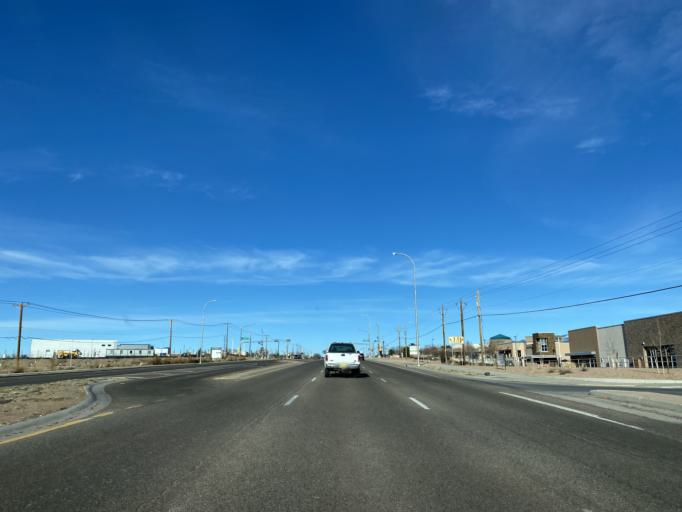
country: US
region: New Mexico
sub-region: Santa Fe County
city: Agua Fria
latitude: 35.6186
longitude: -106.0298
